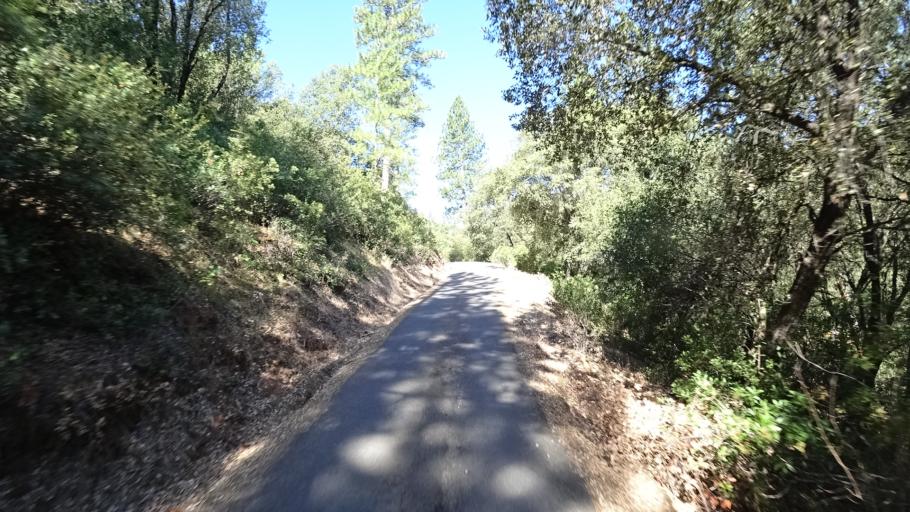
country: US
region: California
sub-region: Calaveras County
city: Mountain Ranch
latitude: 38.1632
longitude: -120.5432
